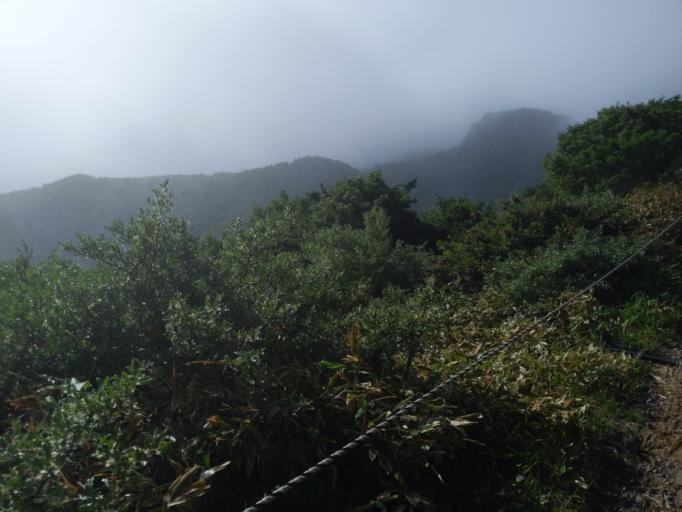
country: KR
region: Jeju-do
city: Seogwipo
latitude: 33.3768
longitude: 126.5308
